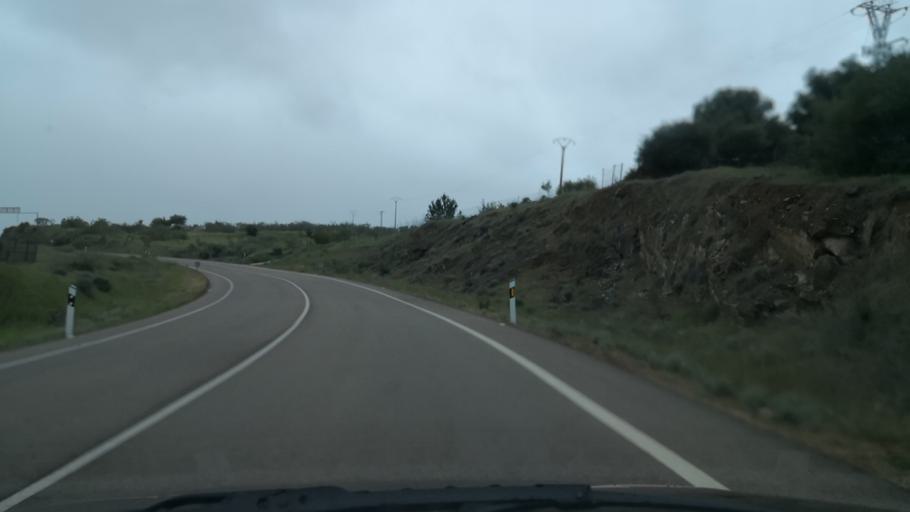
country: ES
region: Extremadura
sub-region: Provincia de Badajoz
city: La Roca de la Sierra
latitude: 39.1125
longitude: -6.6913
